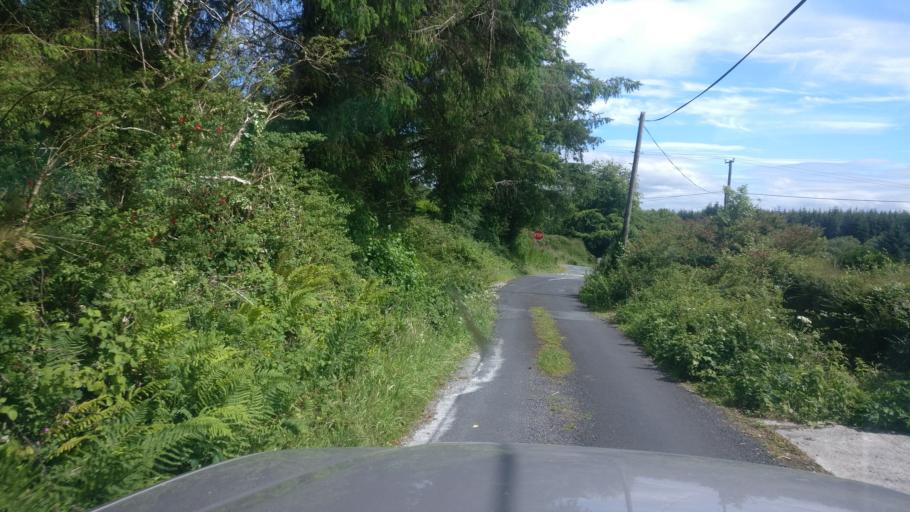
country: IE
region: Connaught
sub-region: County Galway
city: Gort
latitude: 53.0587
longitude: -8.6976
